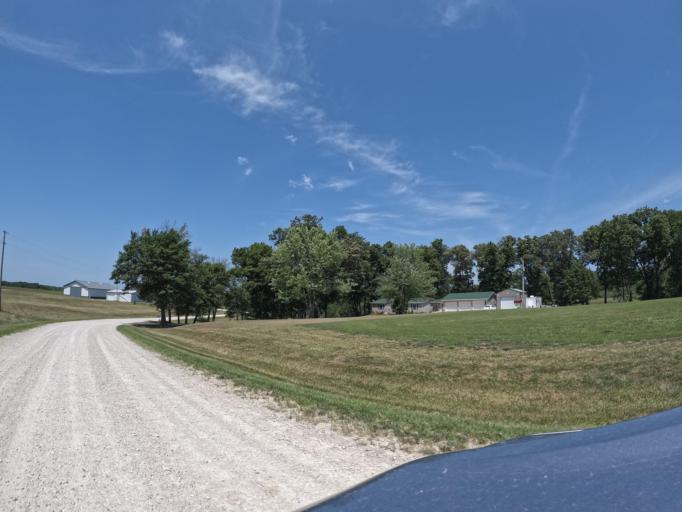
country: US
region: Iowa
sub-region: Henry County
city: Mount Pleasant
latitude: 40.9142
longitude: -91.6588
